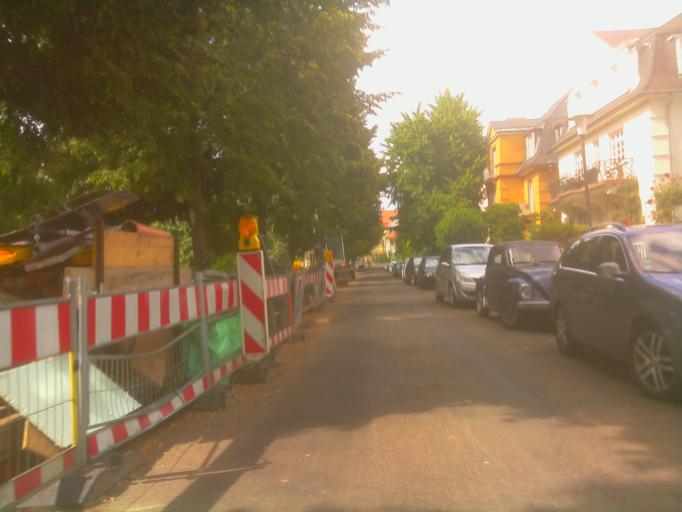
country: DE
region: Baden-Wuerttemberg
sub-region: Karlsruhe Region
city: Heidelberg
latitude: 49.4194
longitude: 8.6871
